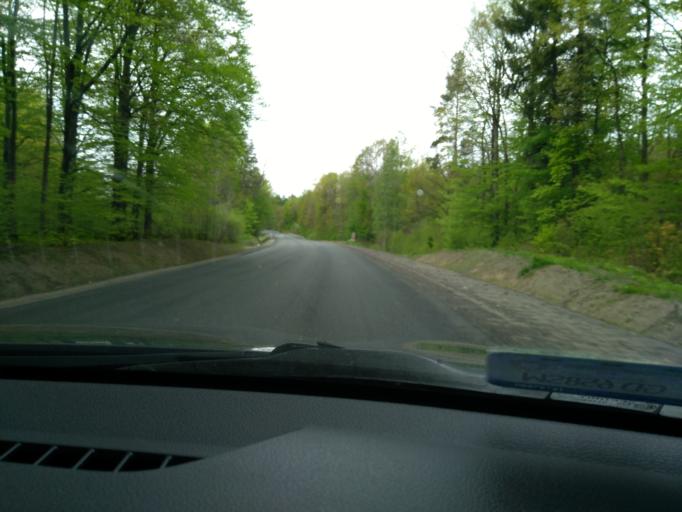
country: PL
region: Pomeranian Voivodeship
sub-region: Powiat kartuski
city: Kartuzy
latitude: 54.3426
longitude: 18.1762
